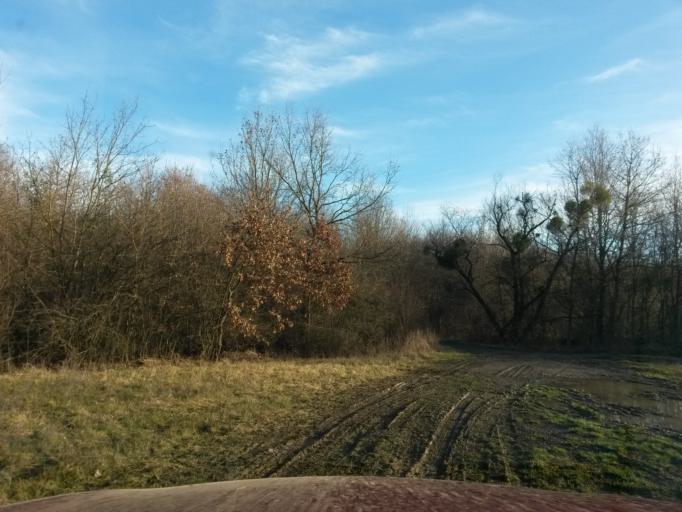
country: SK
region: Kosicky
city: Cierna nad Tisou
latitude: 48.5216
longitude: 22.0244
